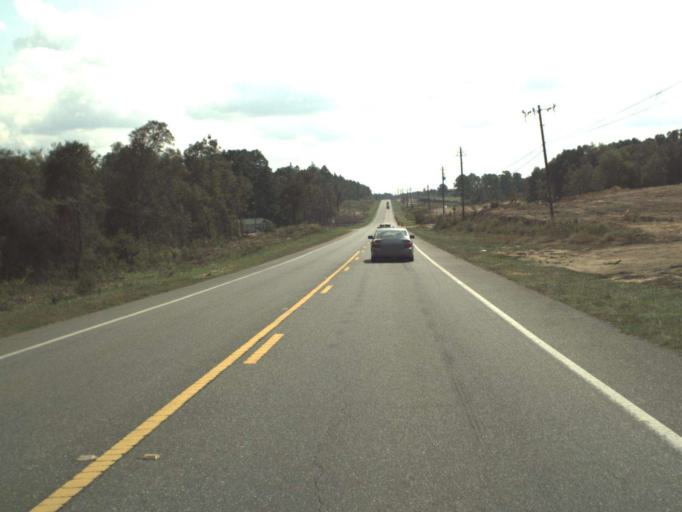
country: US
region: Florida
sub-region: Holmes County
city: Bonifay
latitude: 30.6886
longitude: -85.6864
